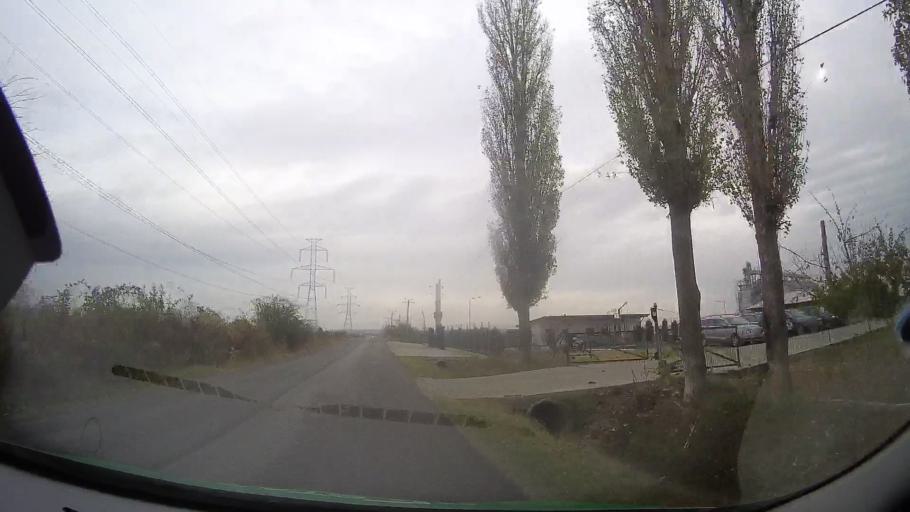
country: RO
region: Prahova
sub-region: Comuna Valea Calugareasca
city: Pantazi
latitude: 44.9289
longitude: 26.1476
